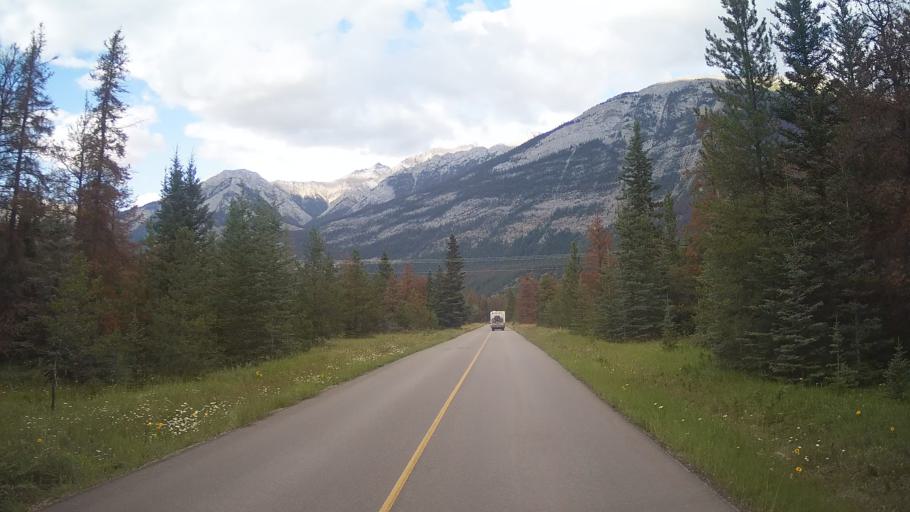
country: CA
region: Alberta
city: Jasper Park Lodge
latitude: 52.9263
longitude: -118.0327
